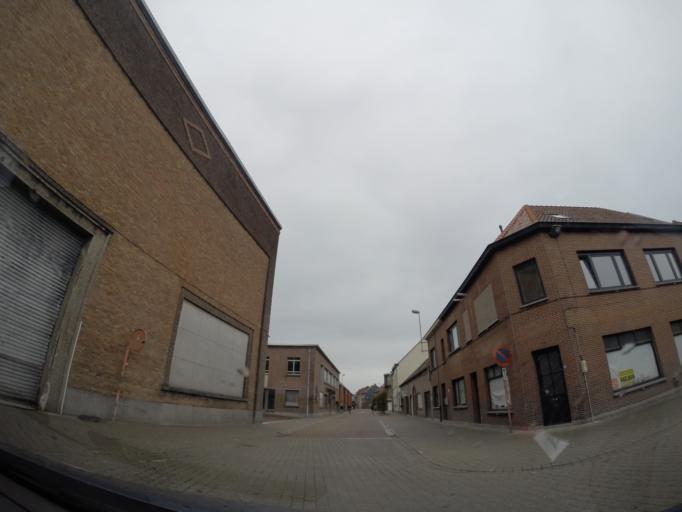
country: BE
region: Flanders
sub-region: Provincie Oost-Vlaanderen
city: Eeklo
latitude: 51.1806
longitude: 3.5691
